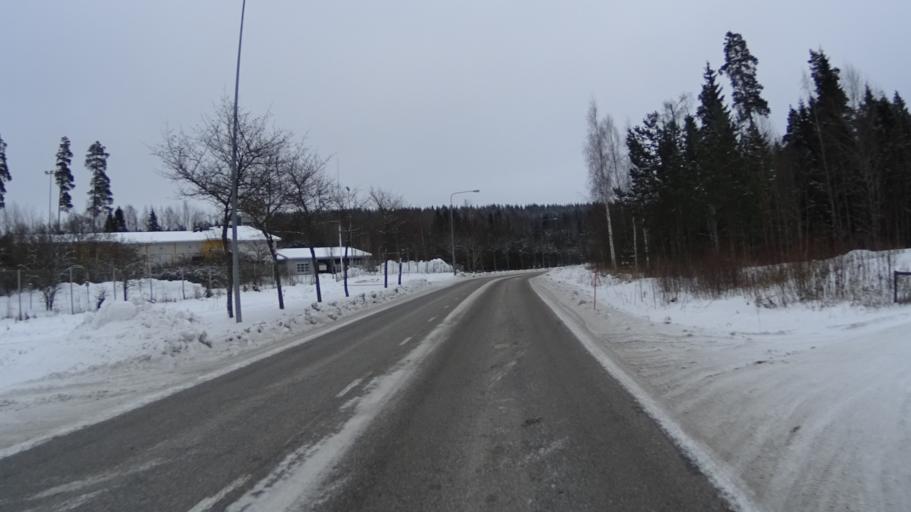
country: FI
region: Uusimaa
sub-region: Helsinki
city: Karkkila
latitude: 60.5290
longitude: 24.2364
